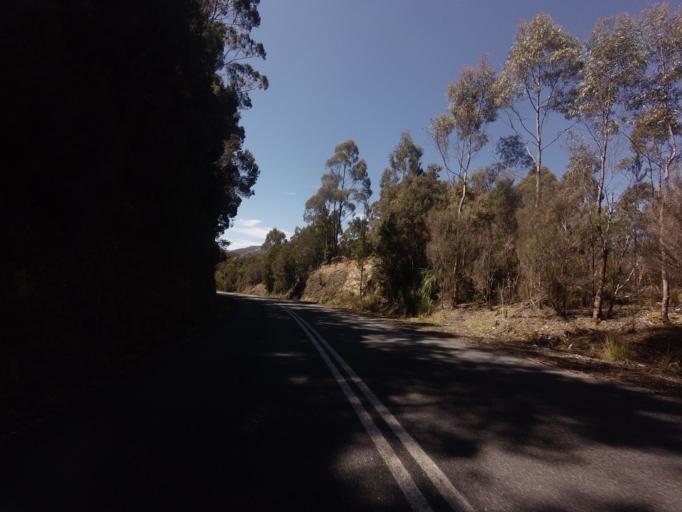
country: AU
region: Tasmania
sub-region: West Coast
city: Queenstown
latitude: -42.7796
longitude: 146.0357
